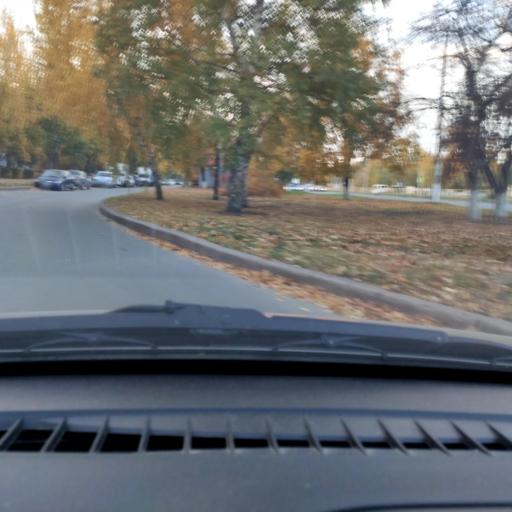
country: RU
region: Samara
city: Tol'yatti
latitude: 53.5351
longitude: 49.2993
